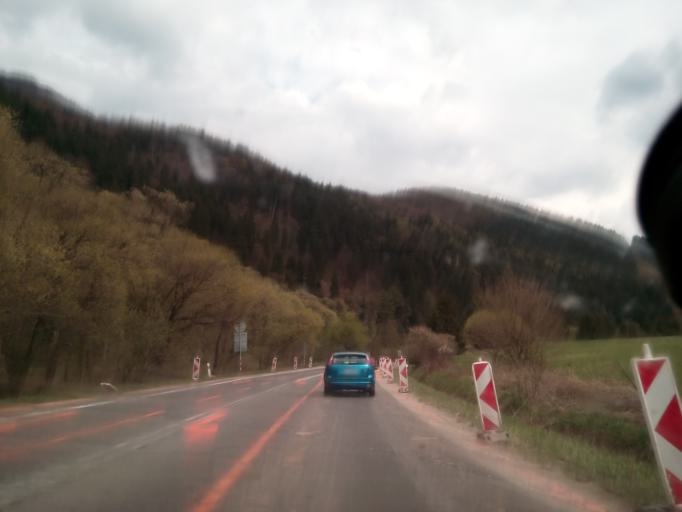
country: SK
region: Zilinsky
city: Ruzomberok
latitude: 49.1194
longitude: 19.2226
